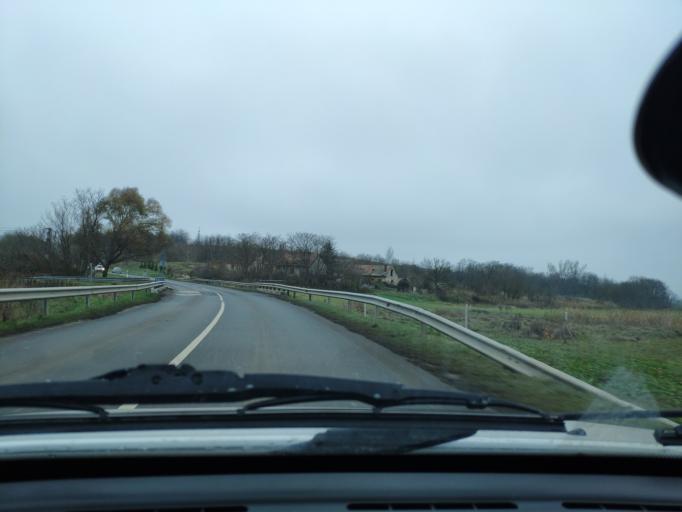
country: HU
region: Pest
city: Biatorbagy
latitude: 47.4504
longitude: 18.8231
